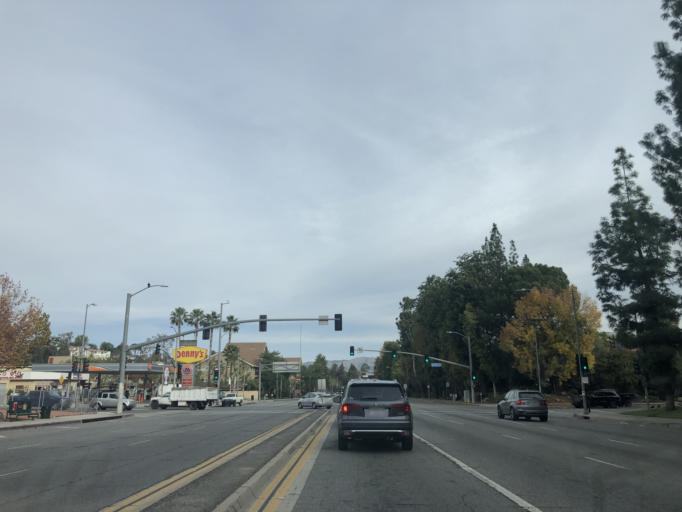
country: US
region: California
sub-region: Los Angeles County
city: Woodland Hills
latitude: 34.1714
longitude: -118.6058
